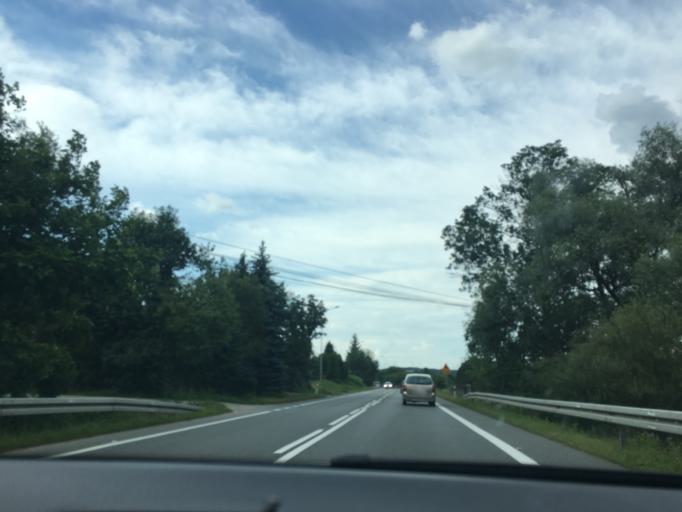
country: PL
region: Subcarpathian Voivodeship
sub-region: Powiat strzyzowski
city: Polomia
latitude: 49.8838
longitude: 21.9008
